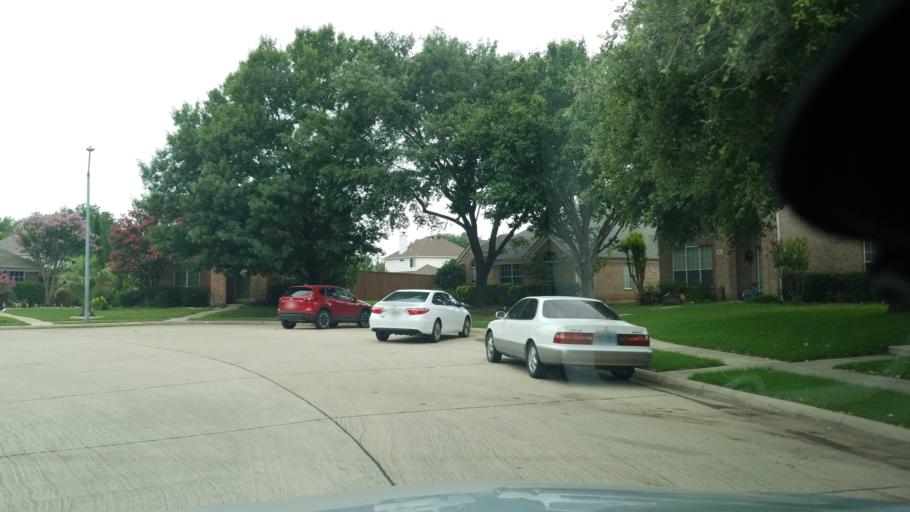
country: US
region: Texas
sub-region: Dallas County
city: Farmers Branch
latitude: 32.9460
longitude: -96.9452
